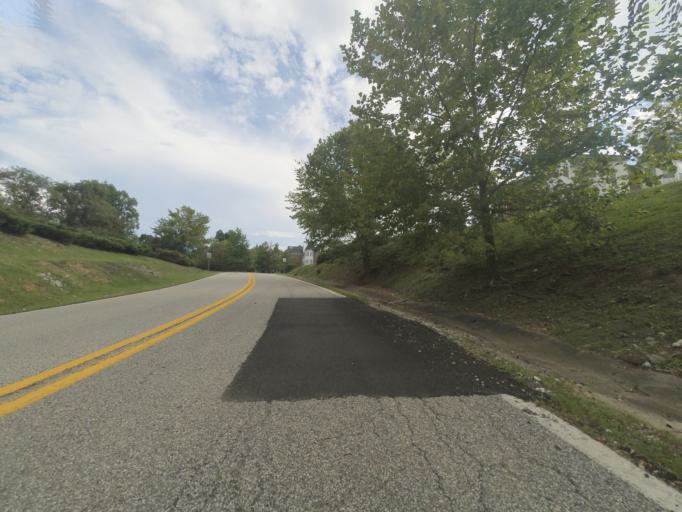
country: US
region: West Virginia
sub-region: Cabell County
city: Huntington
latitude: 38.3922
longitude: -82.4620
